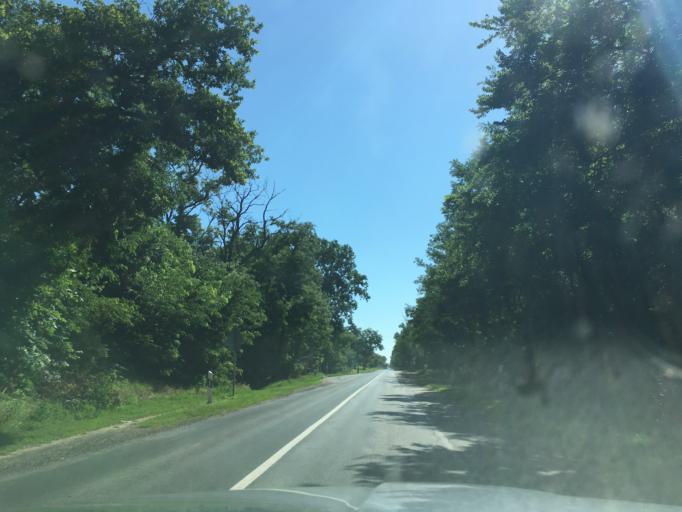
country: HU
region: Hajdu-Bihar
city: Hajdusamson
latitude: 47.5256
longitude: 21.7733
